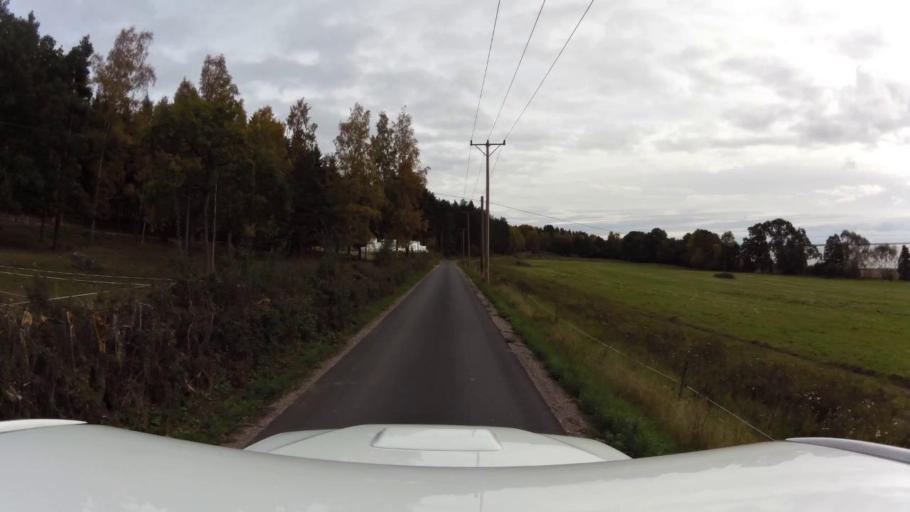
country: SE
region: OEstergoetland
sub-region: Linkopings Kommun
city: Berg
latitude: 58.5115
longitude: 15.5556
